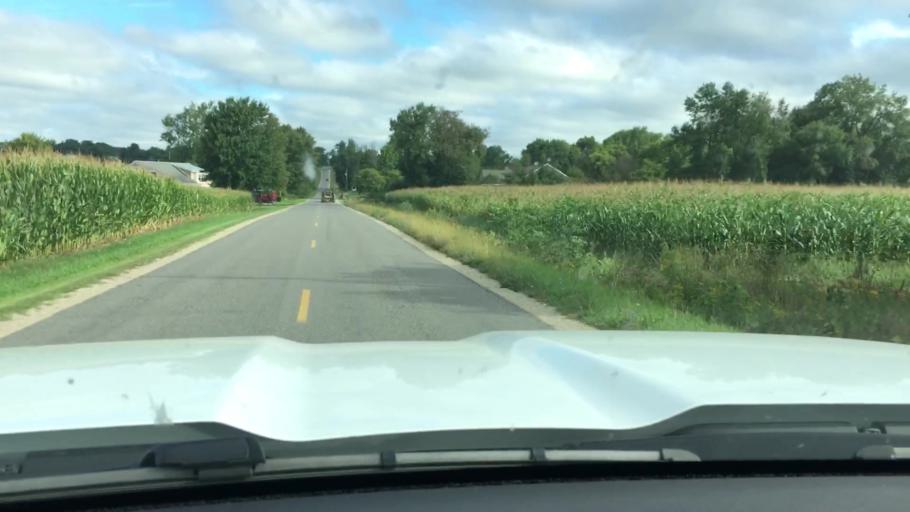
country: US
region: Michigan
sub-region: Kent County
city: Byron Center
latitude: 42.7885
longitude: -85.8026
